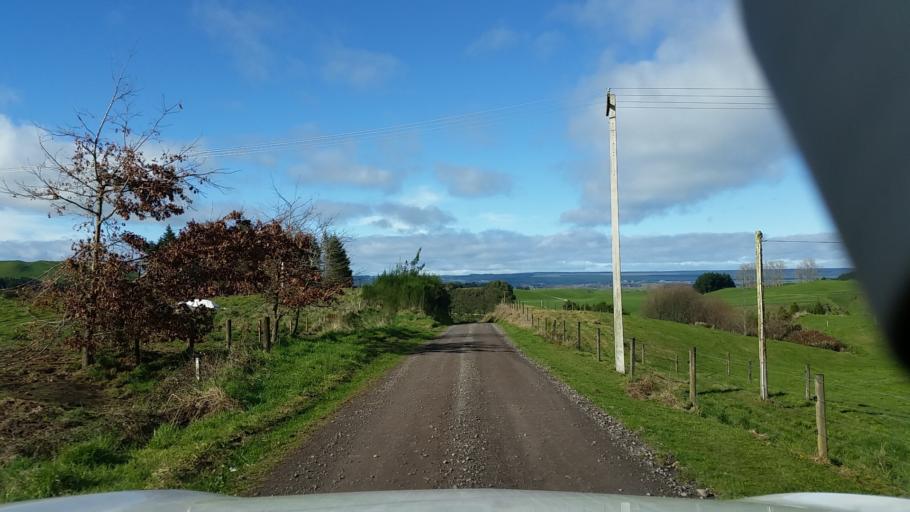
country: NZ
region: Bay of Plenty
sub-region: Rotorua District
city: Rotorua
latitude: -38.4436
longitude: 176.2837
